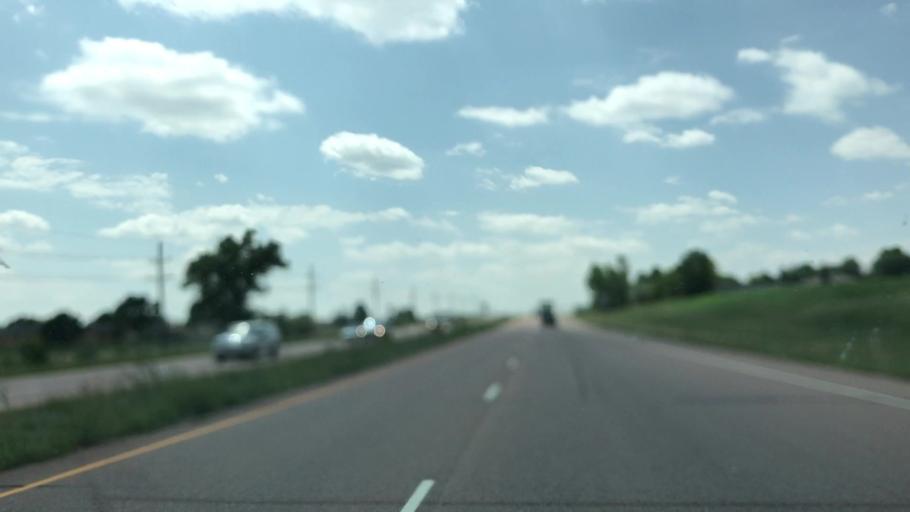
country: US
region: Colorado
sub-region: El Paso County
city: Fort Carson
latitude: 38.7601
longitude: -104.8121
